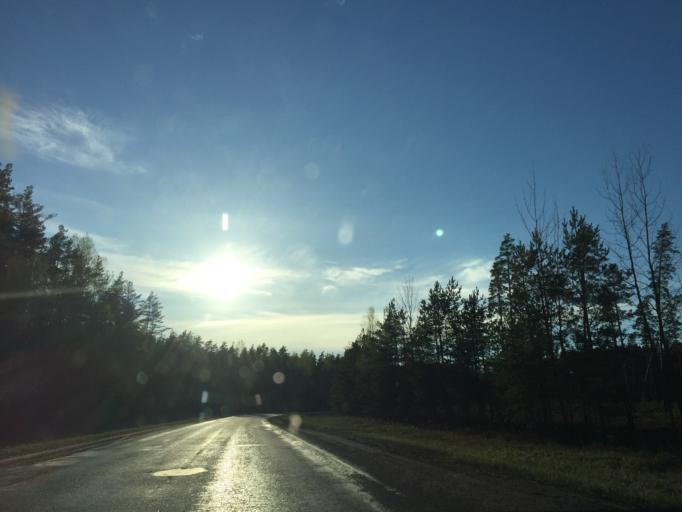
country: LV
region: Strenci
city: Seda
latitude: 57.6257
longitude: 25.7484
